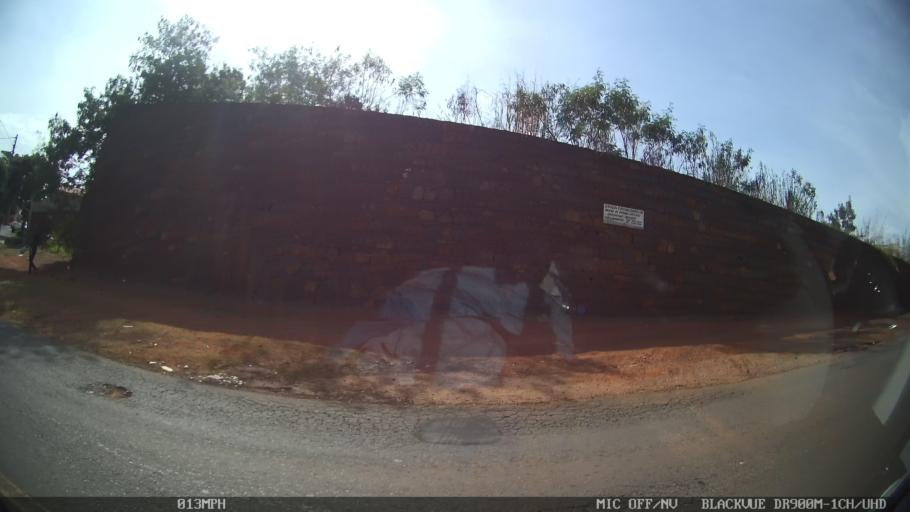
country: BR
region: Sao Paulo
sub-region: Piracicaba
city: Piracicaba
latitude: -22.7625
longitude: -47.5982
